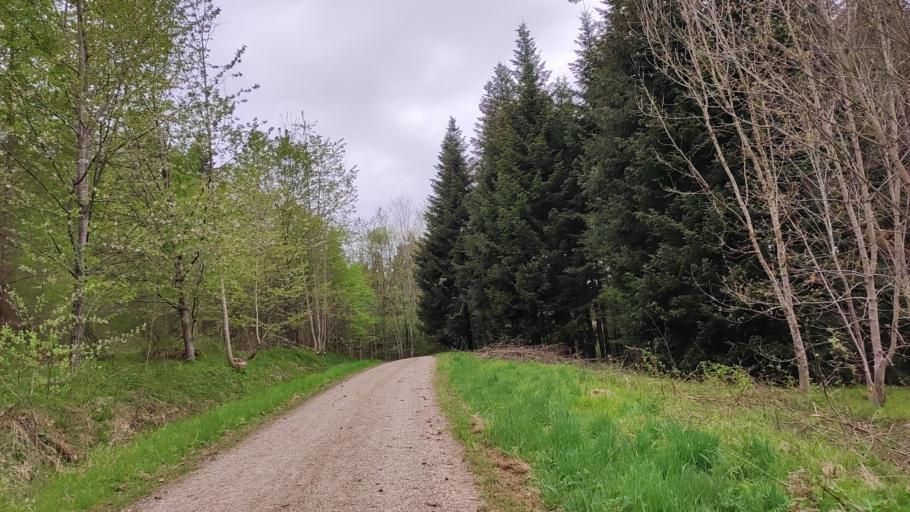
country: DE
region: Bavaria
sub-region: Swabia
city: Altenmunster
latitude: 48.4866
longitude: 10.5639
